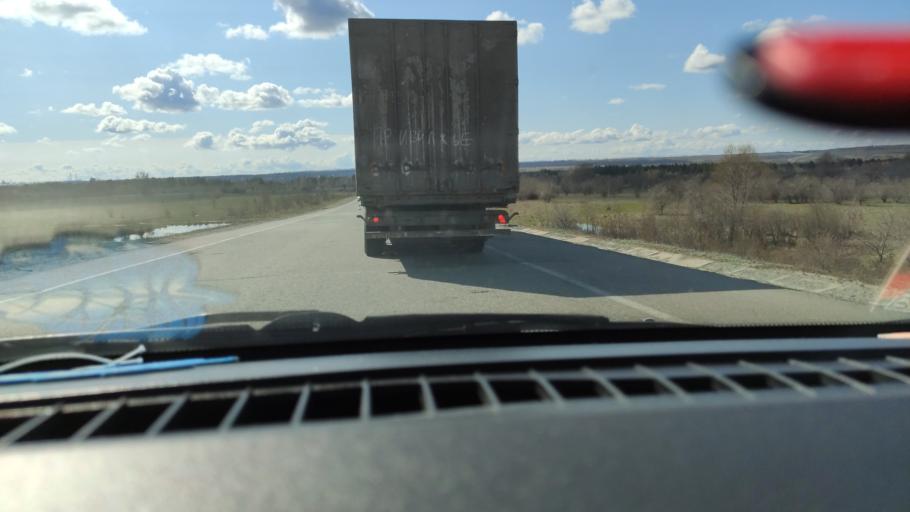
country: RU
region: Samara
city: Varlamovo
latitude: 53.1586
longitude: 48.2841
